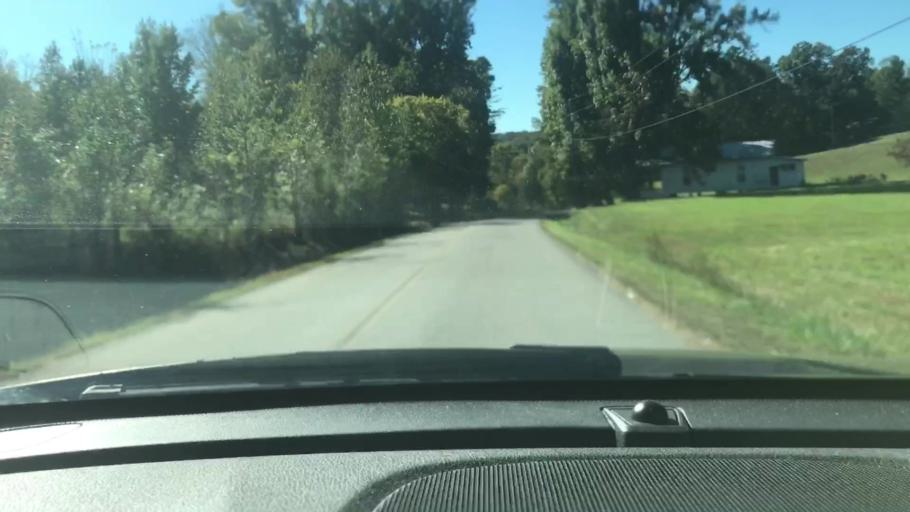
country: US
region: Tennessee
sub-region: Dickson County
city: Charlotte
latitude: 36.1805
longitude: -87.3018
